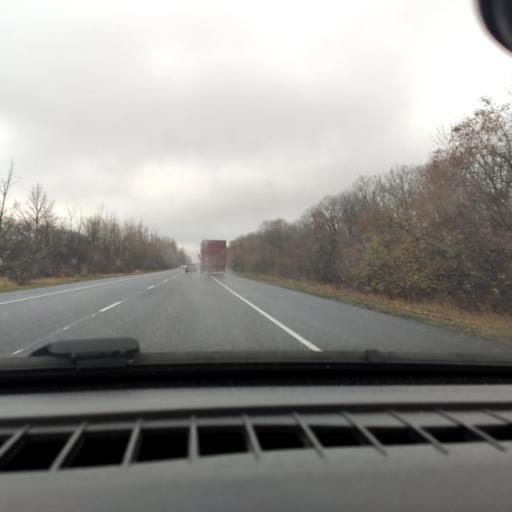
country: RU
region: Voronezj
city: Kolodeznyy
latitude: 51.2429
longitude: 39.0565
